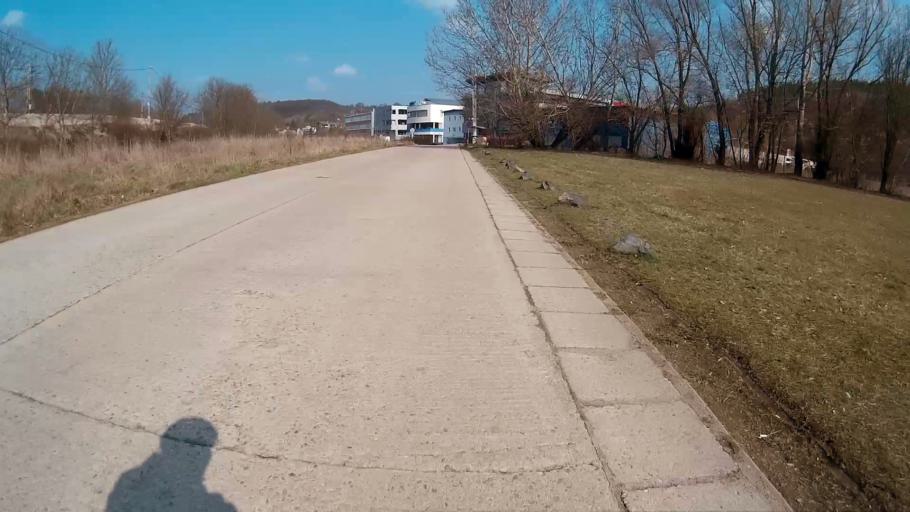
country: CZ
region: South Moravian
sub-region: Mesto Brno
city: Mokra Hora
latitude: 49.2543
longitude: 16.5916
